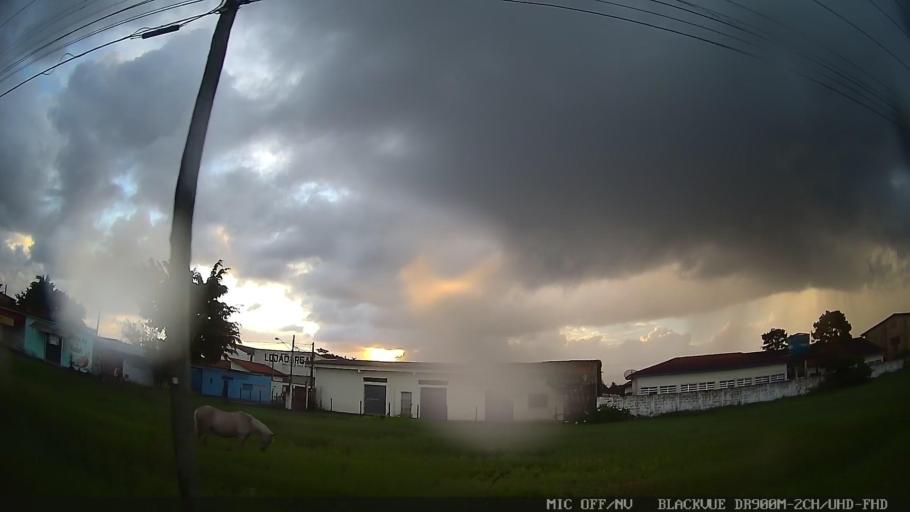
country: BR
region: Sao Paulo
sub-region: Itanhaem
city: Itanhaem
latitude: -24.1540
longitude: -46.7799
